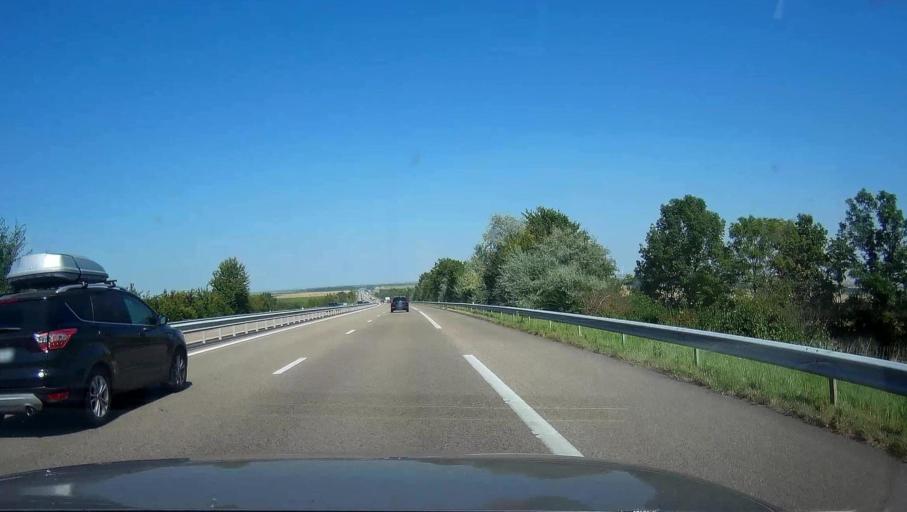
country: FR
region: Champagne-Ardenne
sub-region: Departement de l'Aube
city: Creney-pres-Troyes
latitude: 48.3795
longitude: 4.1570
